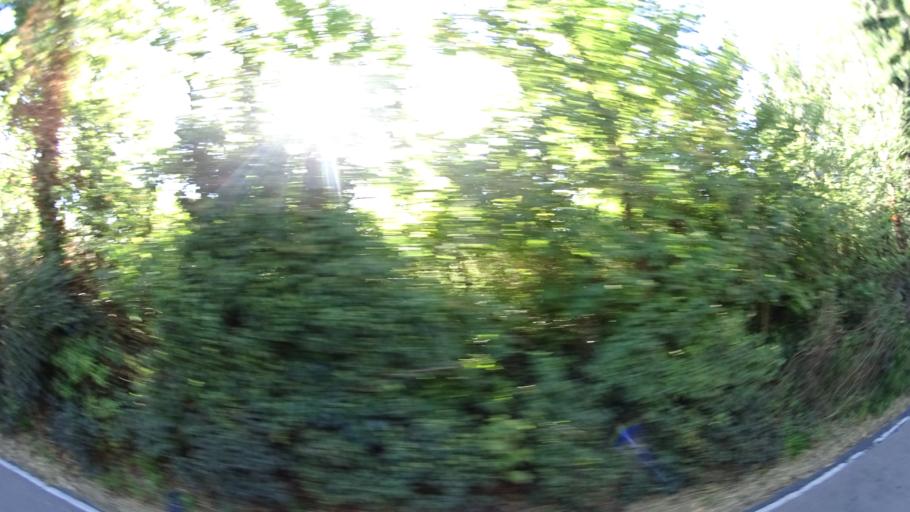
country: GB
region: England
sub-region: Hampshire
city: Romsey
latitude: 51.0795
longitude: -1.4860
